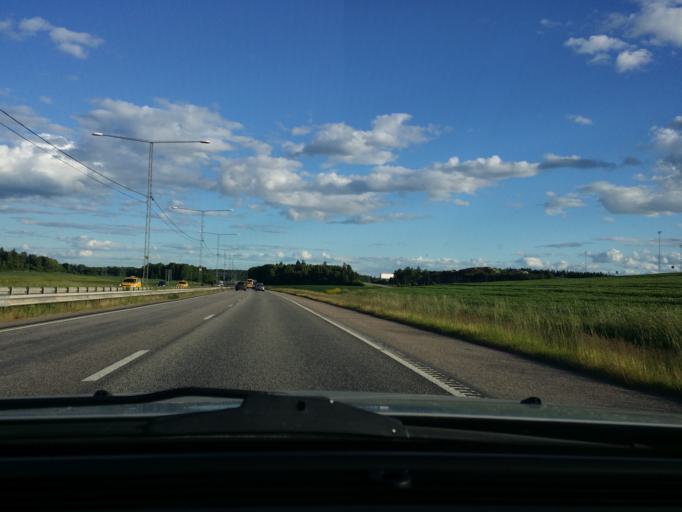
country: SE
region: Stockholm
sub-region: Sigtuna Kommun
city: Rosersberg
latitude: 59.5665
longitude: 17.8972
